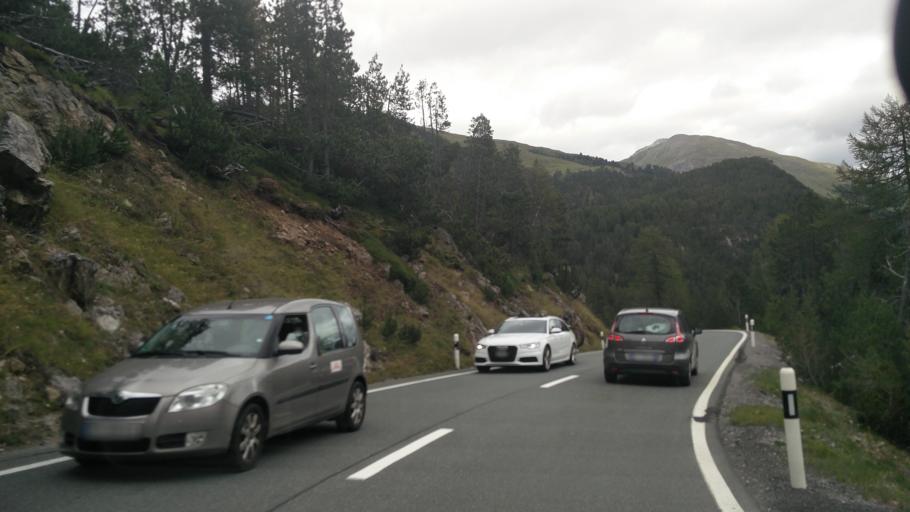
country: IT
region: Lombardy
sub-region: Provincia di Sondrio
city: Isolaccia
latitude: 46.6355
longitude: 10.3030
